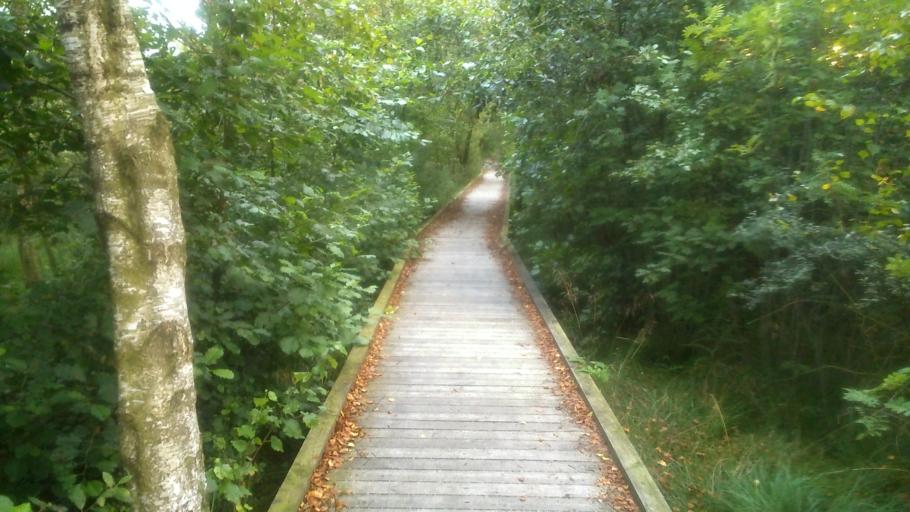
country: DK
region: Central Jutland
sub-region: Ringkobing-Skjern Kommune
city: Skjern
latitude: 56.0089
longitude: 8.4730
